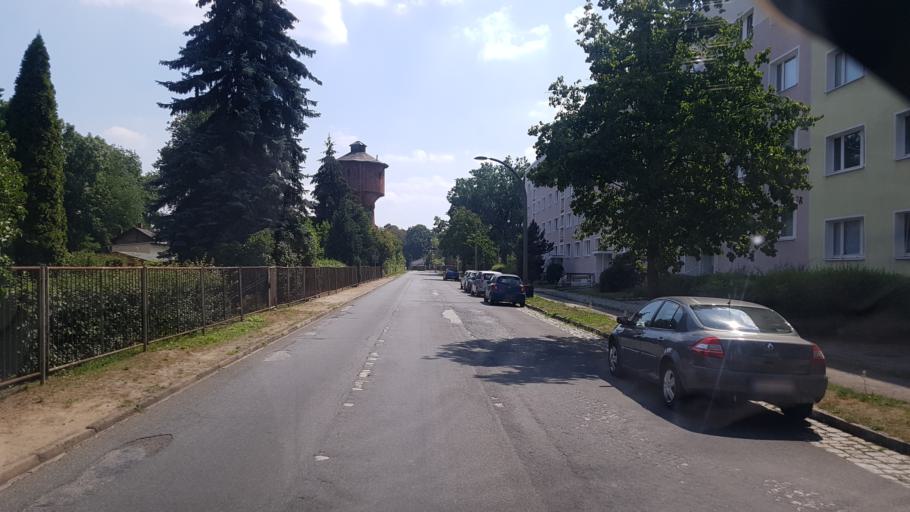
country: DE
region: Brandenburg
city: Spremberg
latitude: 51.5769
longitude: 14.3950
